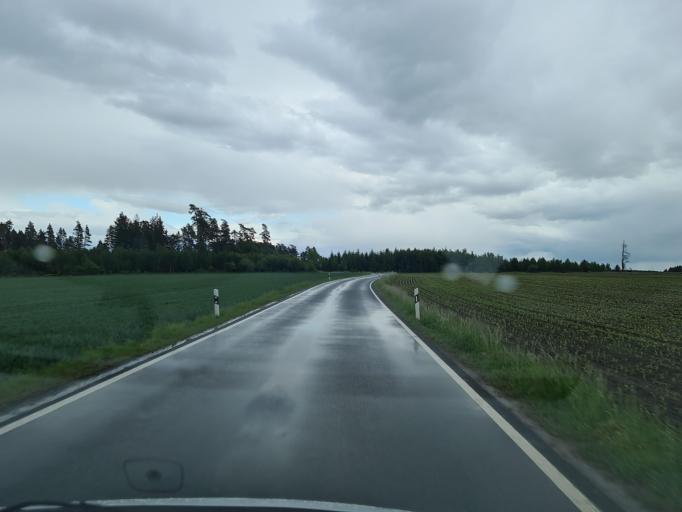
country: DE
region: Thuringia
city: Tanna
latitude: 50.5112
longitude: 11.8929
